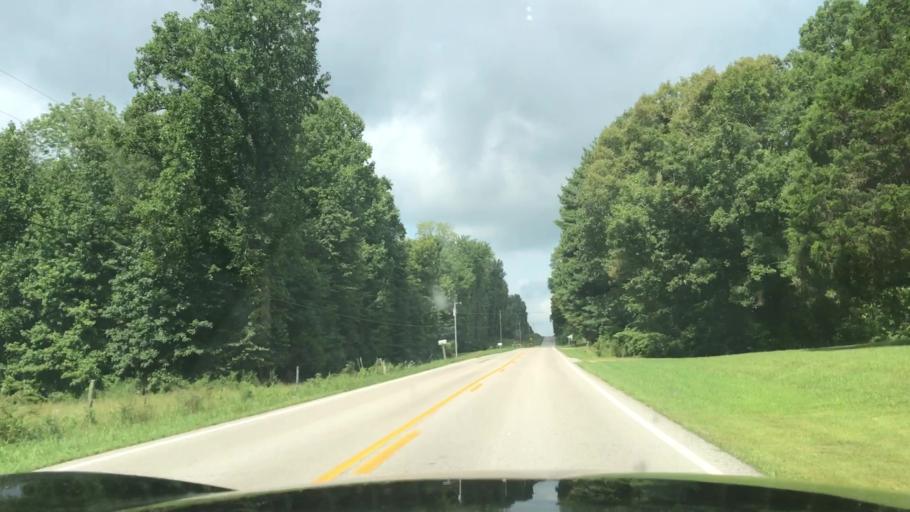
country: US
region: Kentucky
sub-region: Butler County
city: Morgantown
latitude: 37.1720
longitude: -86.8238
